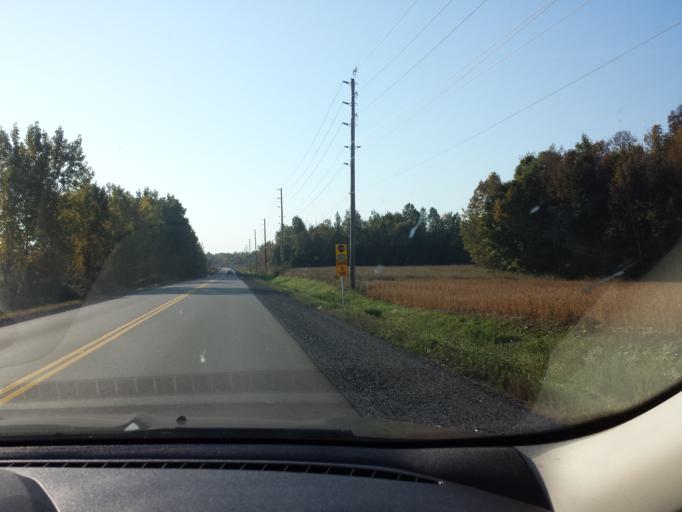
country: CA
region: Ontario
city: Prescott
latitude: 45.0273
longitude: -75.5825
